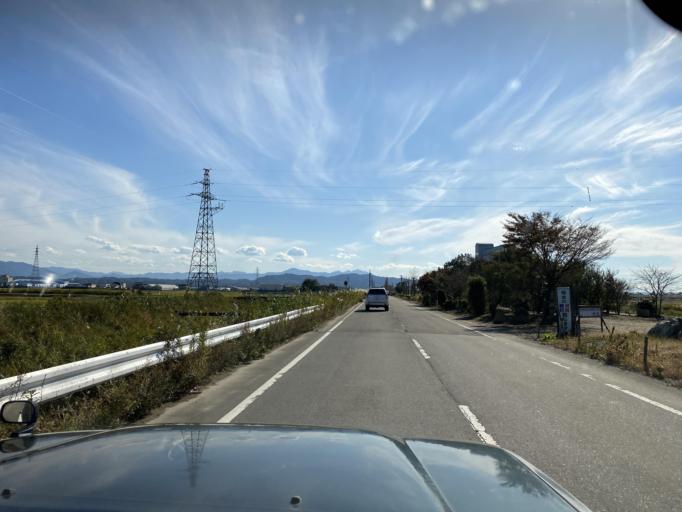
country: JP
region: Niigata
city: Niitsu-honcho
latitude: 37.7972
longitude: 139.0776
